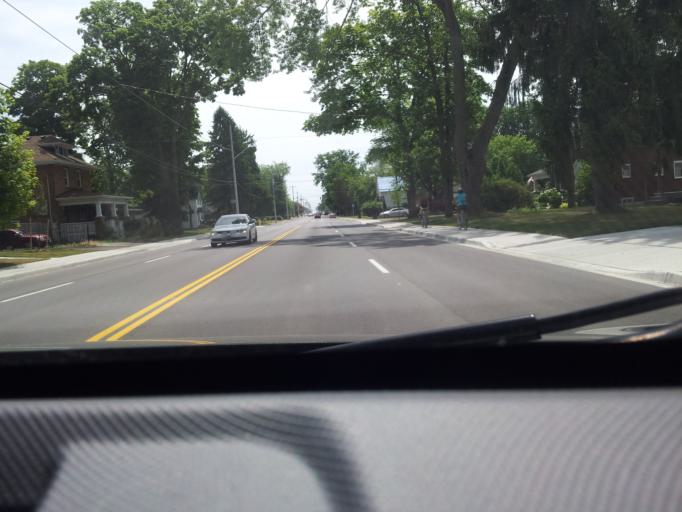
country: CA
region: Ontario
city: Norfolk County
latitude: 42.7913
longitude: -80.2102
